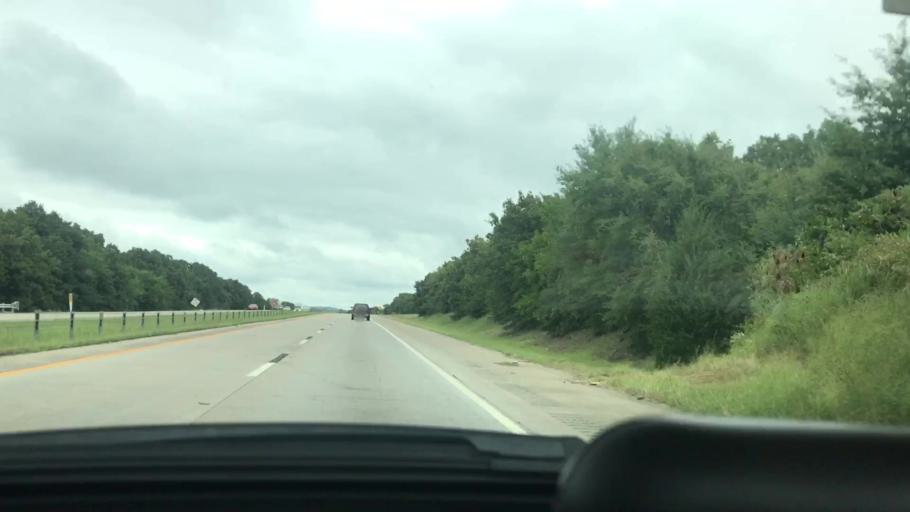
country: US
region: Oklahoma
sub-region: Pittsburg County
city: Krebs
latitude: 35.0000
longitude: -95.7200
